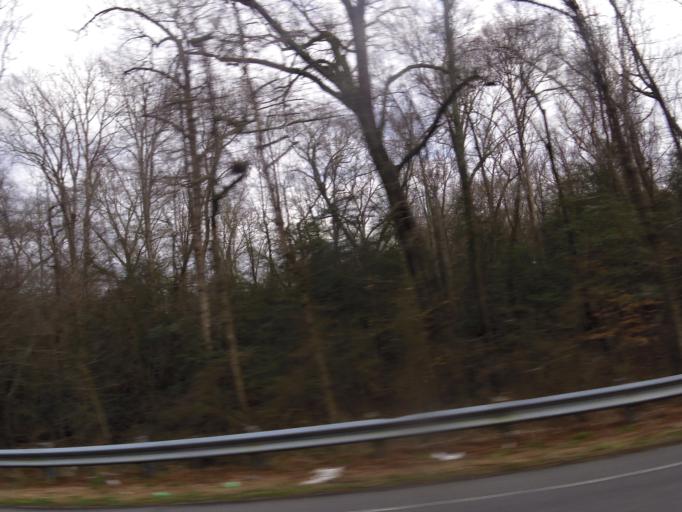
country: US
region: North Carolina
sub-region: Edgecombe County
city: Pinetops
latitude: 35.8198
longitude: -77.6600
